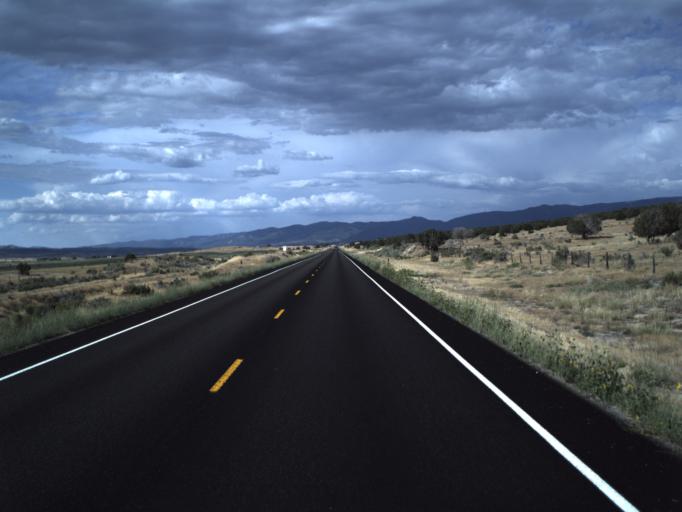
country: US
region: Utah
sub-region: Sanpete County
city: Moroni
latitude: 39.4591
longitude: -111.5385
